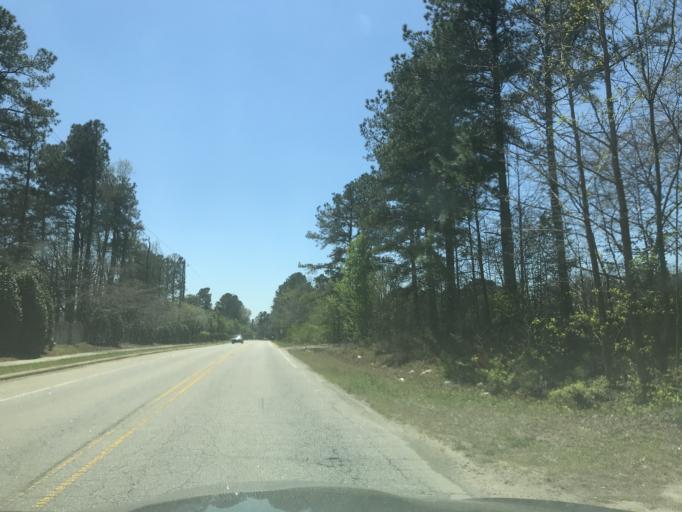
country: US
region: North Carolina
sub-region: Wake County
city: Knightdale
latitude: 35.8528
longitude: -78.5553
